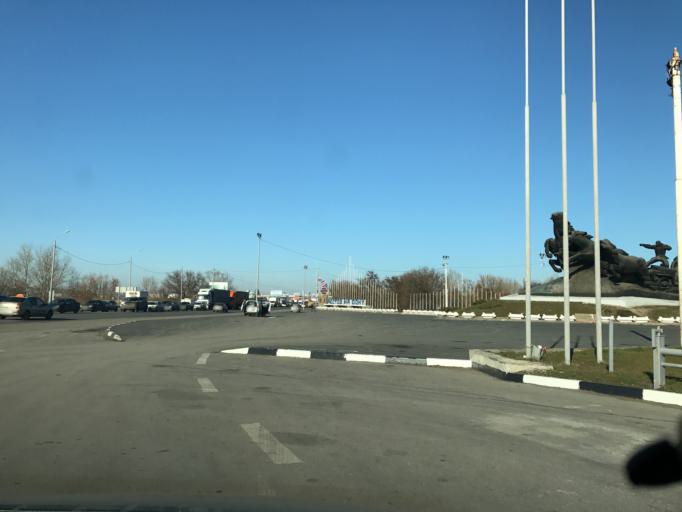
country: RU
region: Rostov
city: Bataysk
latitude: 47.1833
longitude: 39.7388
